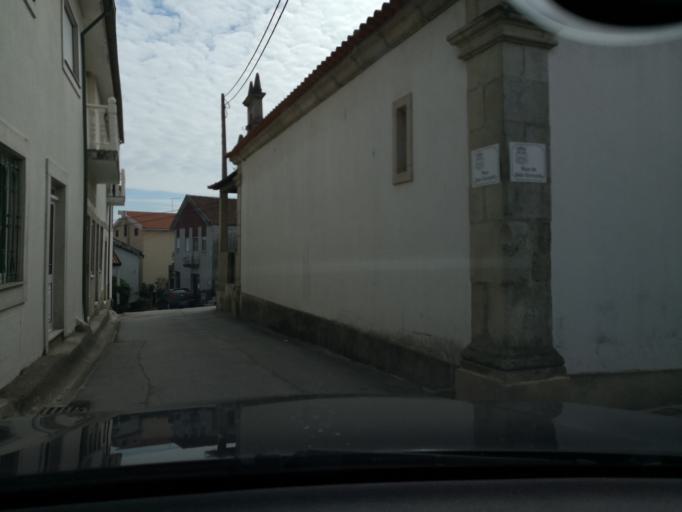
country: PT
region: Vila Real
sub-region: Vila Real
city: Vila Real
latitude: 41.2256
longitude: -7.6974
